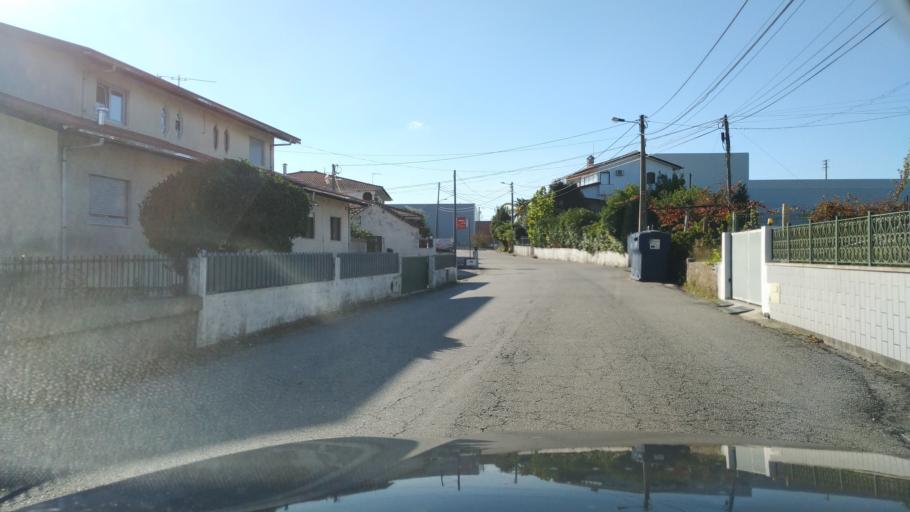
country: PT
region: Aveiro
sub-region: Vale de Cambra
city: Vale de Cambra
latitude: 40.8708
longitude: -8.4145
